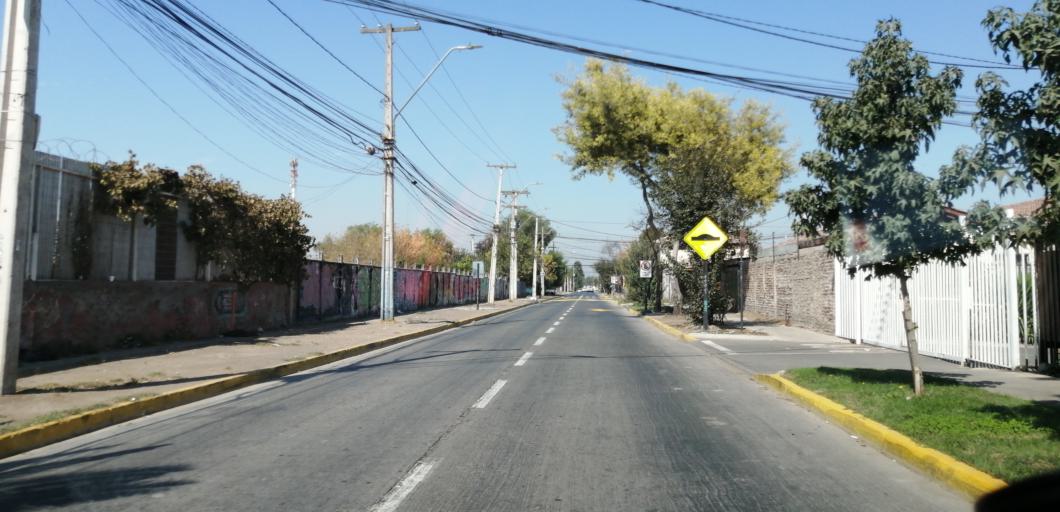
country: CL
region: Santiago Metropolitan
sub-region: Provincia de Santiago
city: Lo Prado
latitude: -33.4543
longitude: -70.7445
